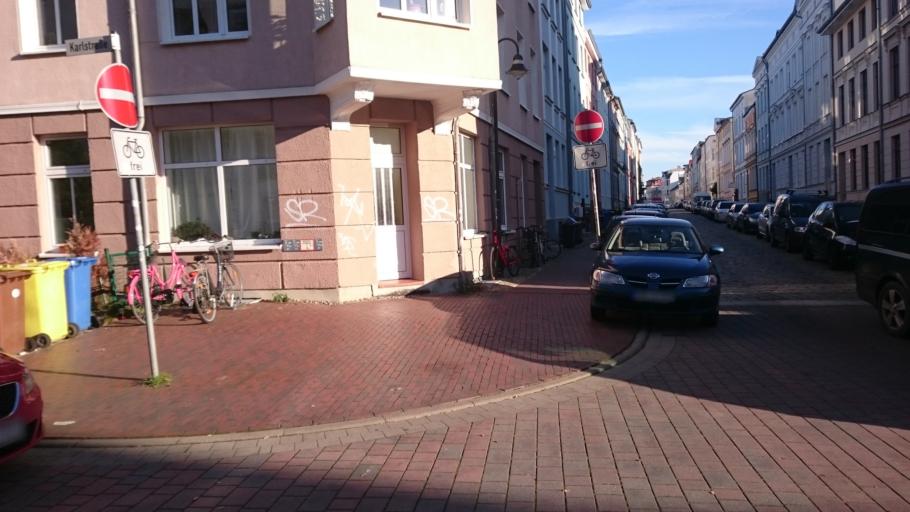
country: DE
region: Mecklenburg-Vorpommern
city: Rostock
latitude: 54.0846
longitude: 12.1280
